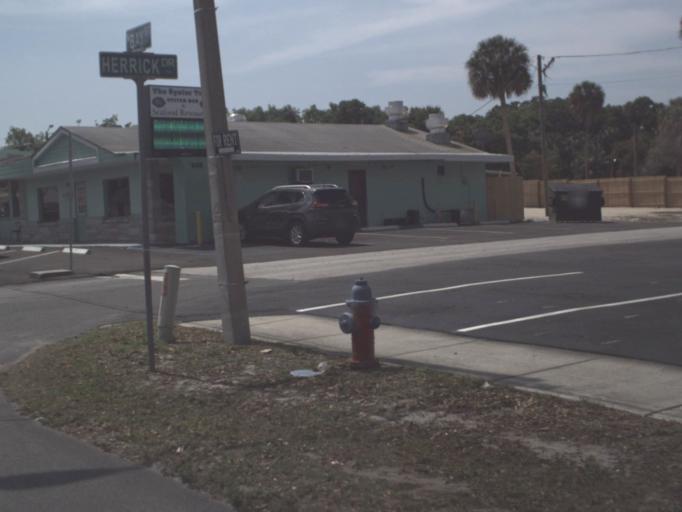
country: US
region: Florida
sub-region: Lake County
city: Eustis
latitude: 28.8630
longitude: -81.6862
